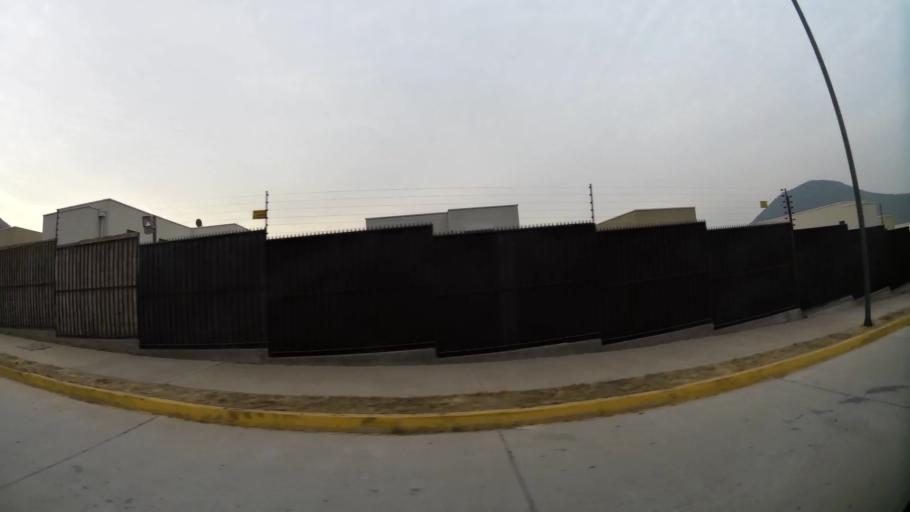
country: CL
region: Santiago Metropolitan
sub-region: Provincia de Chacabuco
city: Chicureo Abajo
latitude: -33.3234
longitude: -70.6494
